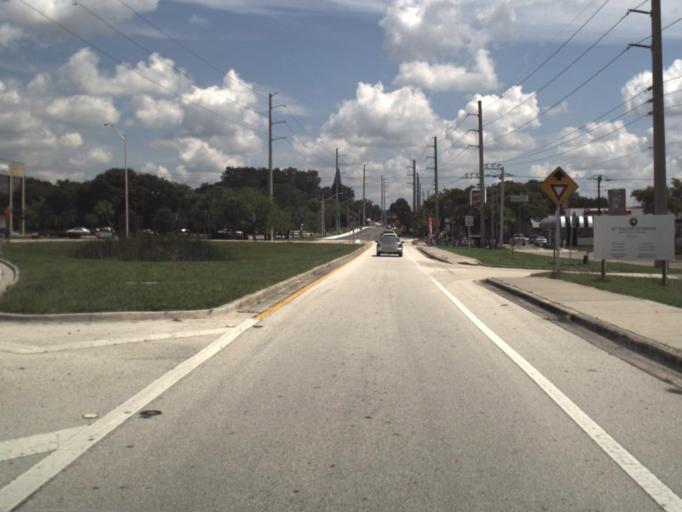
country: US
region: Florida
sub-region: Manatee County
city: West Samoset
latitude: 27.4624
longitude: -82.5644
